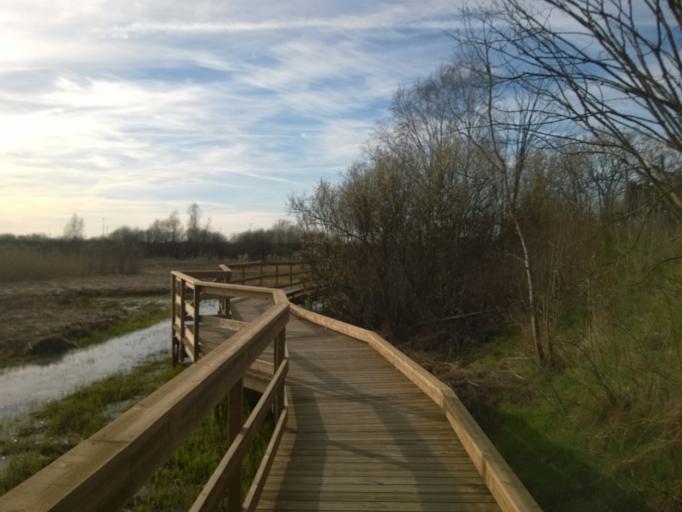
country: SE
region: Skane
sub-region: Kristianstads Kommun
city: Kristianstad
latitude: 56.0360
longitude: 14.1444
